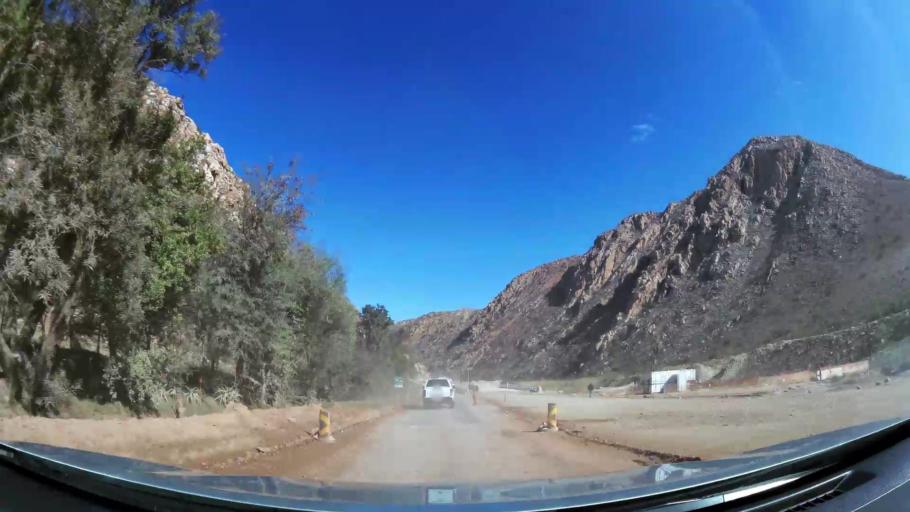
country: ZA
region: Western Cape
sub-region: Cape Winelands District Municipality
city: Ashton
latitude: -33.7933
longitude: 20.1067
